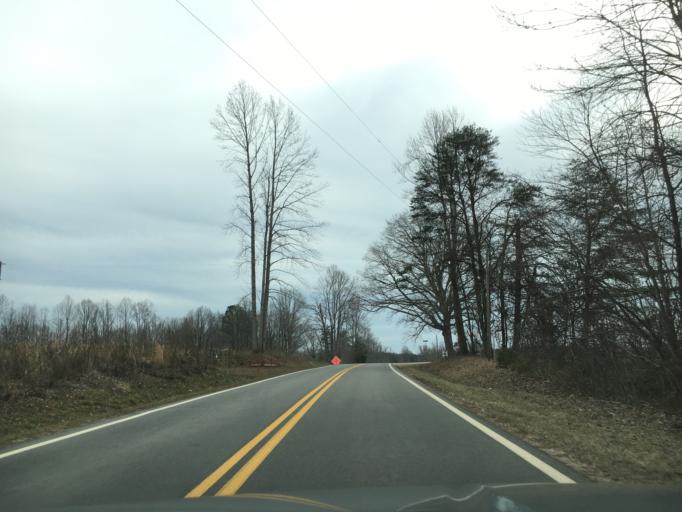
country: US
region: Virginia
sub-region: Charlotte County
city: Charlotte Court House
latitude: 37.1022
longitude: -78.7455
